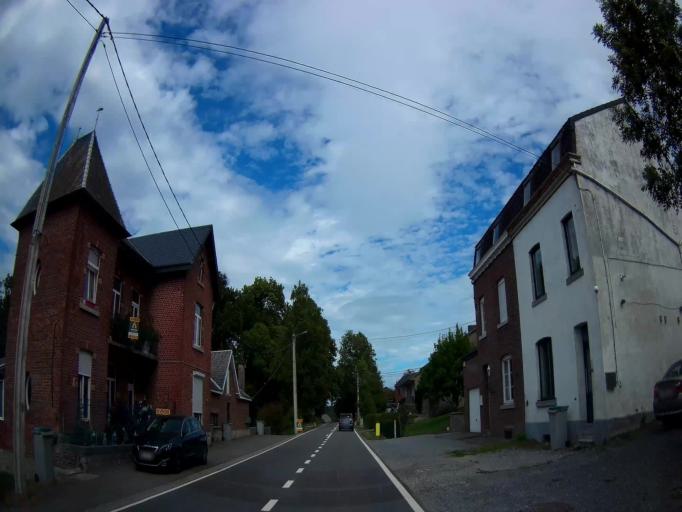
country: BE
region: Wallonia
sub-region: Province de Liege
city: Hamoir
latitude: 50.3711
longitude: 5.5191
